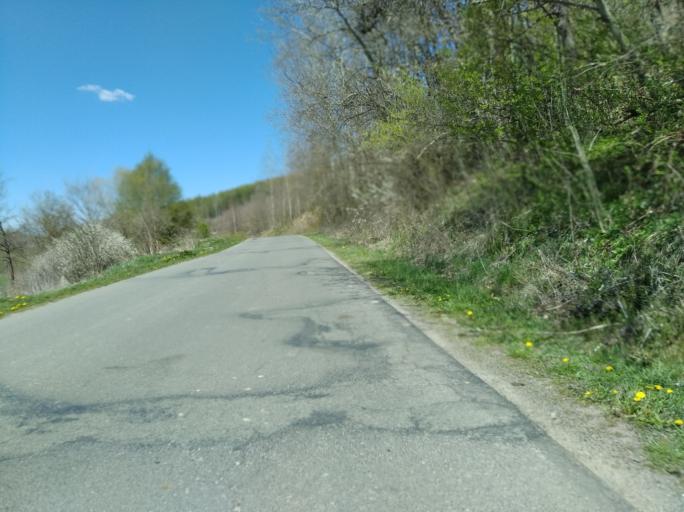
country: PL
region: Subcarpathian Voivodeship
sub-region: Powiat brzozowski
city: Dydnia
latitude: 49.7034
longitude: 22.1523
